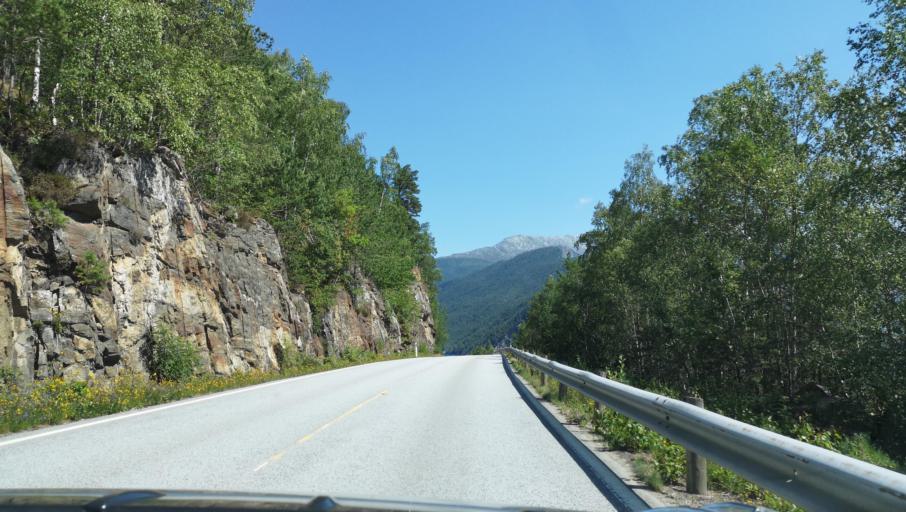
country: NO
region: Hordaland
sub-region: Ulvik
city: Ulvik
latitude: 60.4870
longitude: 6.8822
